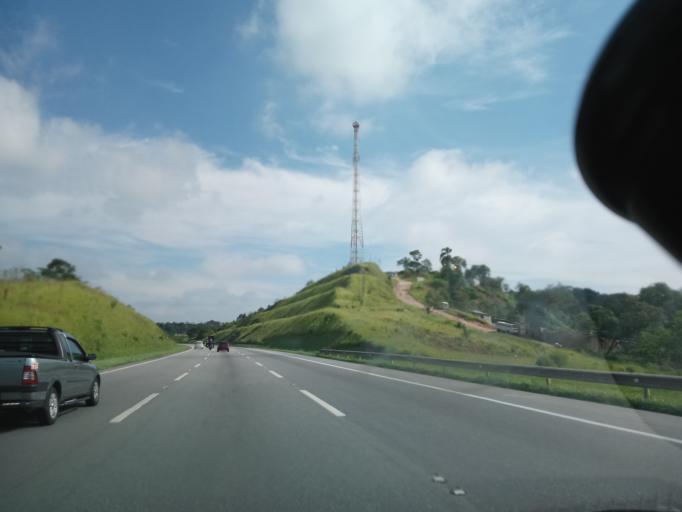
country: BR
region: Sao Paulo
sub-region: Itapecerica Da Serra
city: Itapecerica da Serra
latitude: -23.7191
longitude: -46.8060
